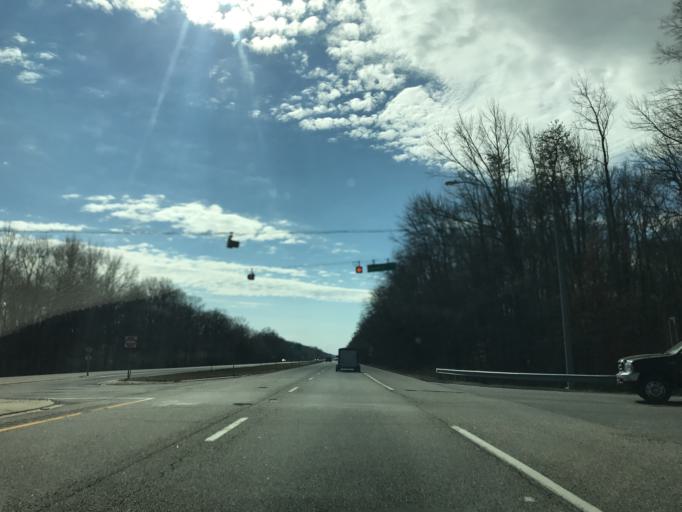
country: US
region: Delaware
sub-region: New Castle County
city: Townsend
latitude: 39.3200
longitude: -75.8468
